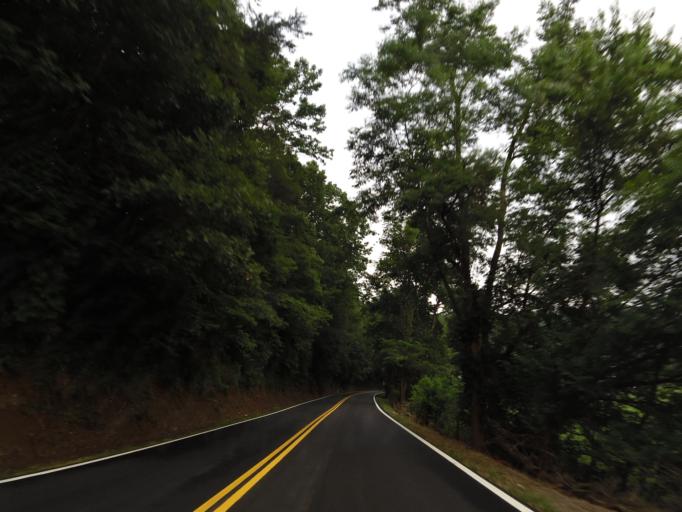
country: US
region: Tennessee
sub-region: Sevier County
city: Sevierville
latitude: 35.8322
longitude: -83.6334
